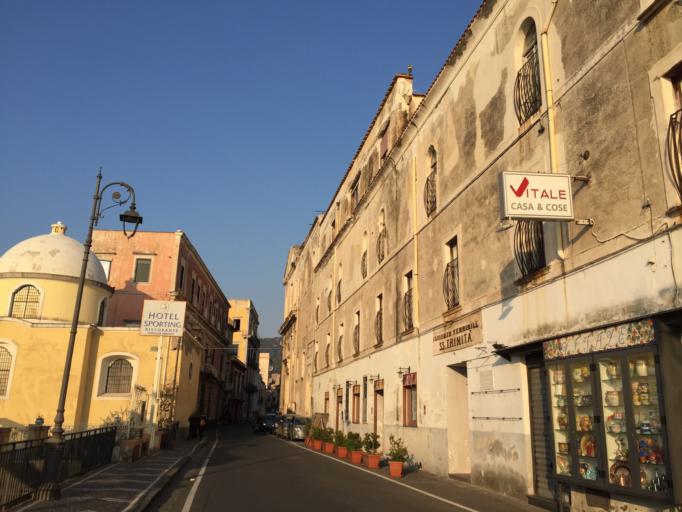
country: IT
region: Campania
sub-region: Provincia di Napoli
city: Vico Equense
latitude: 40.6629
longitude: 14.4238
